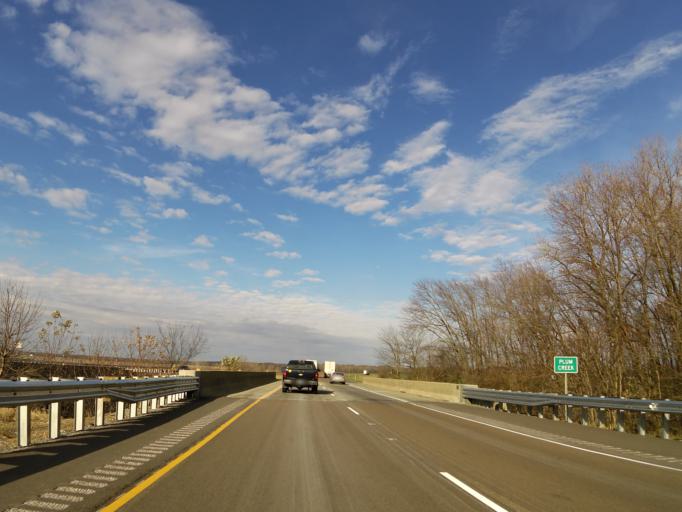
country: US
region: Illinois
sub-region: Washington County
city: Okawville
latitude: 38.4569
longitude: -89.5624
